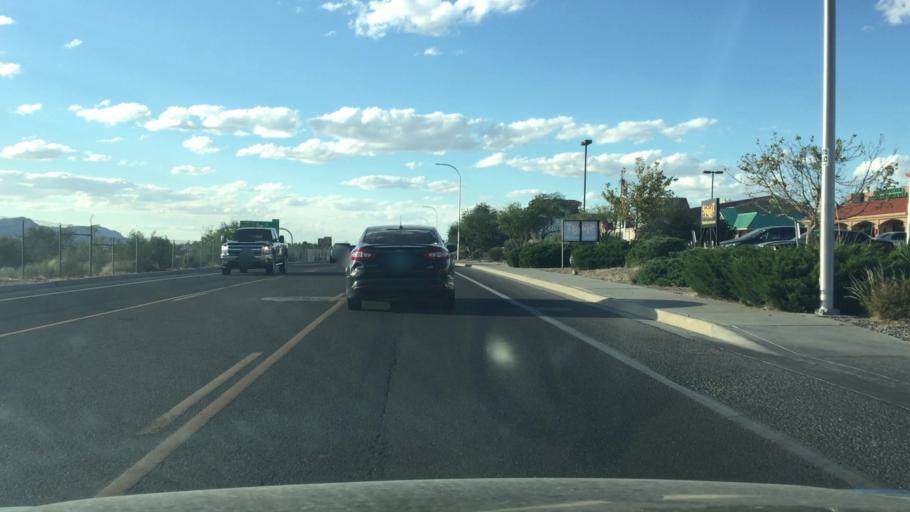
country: US
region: New Mexico
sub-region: Dona Ana County
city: Las Cruces
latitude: 32.3309
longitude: -106.7571
